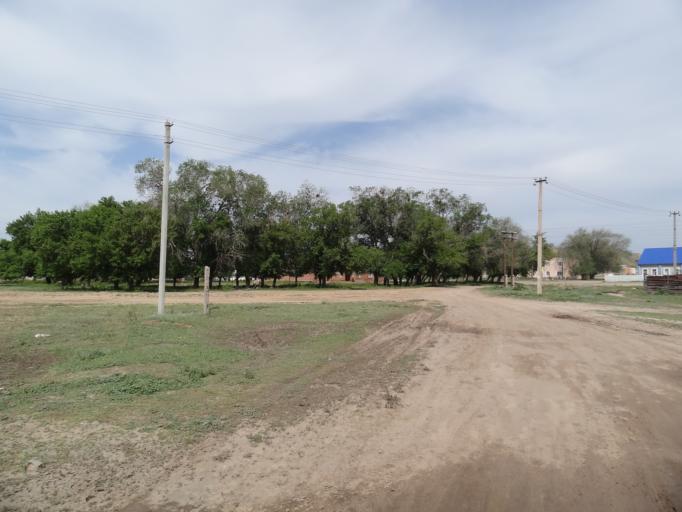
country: RU
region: Saratov
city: Privolzhskiy
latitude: 51.2037
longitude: 45.9155
